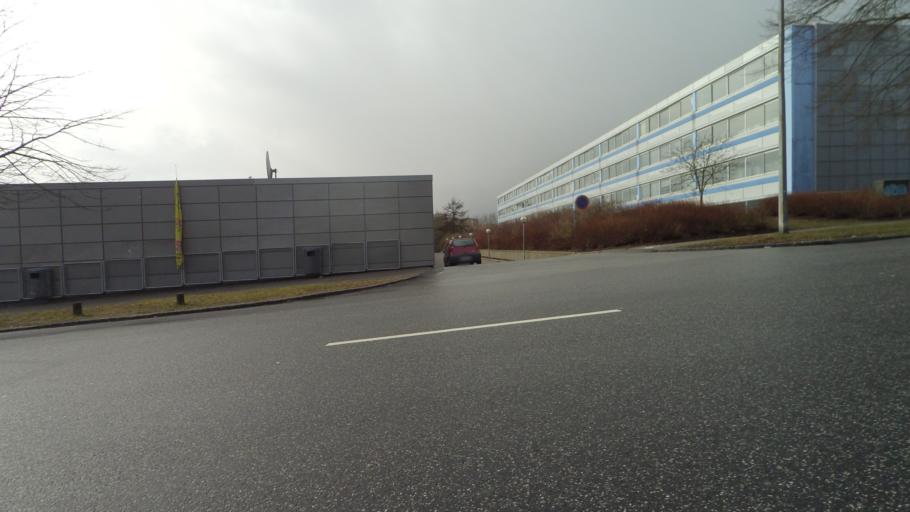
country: DK
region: Central Jutland
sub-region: Arhus Kommune
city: Arhus
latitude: 56.1645
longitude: 10.1751
